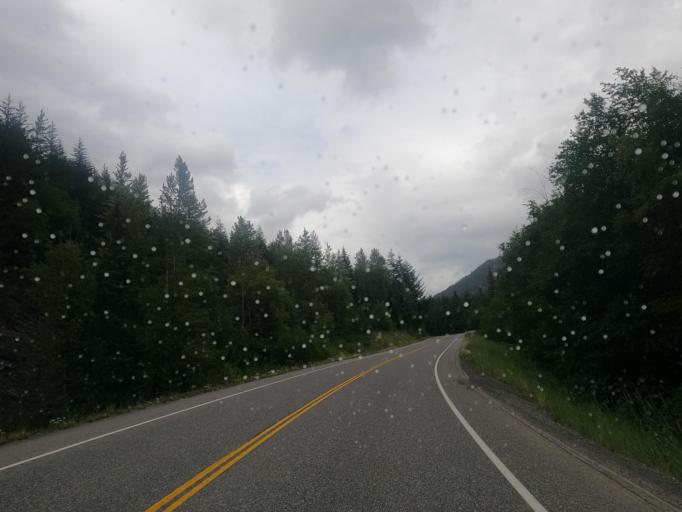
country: CA
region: British Columbia
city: Lillooet
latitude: 50.5012
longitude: -122.1845
